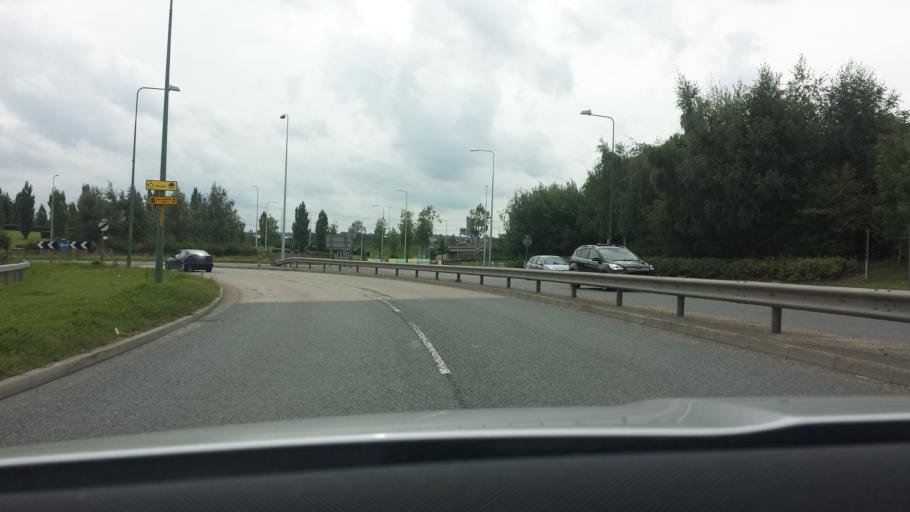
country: GB
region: England
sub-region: Kent
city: Swanscombe
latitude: 51.4329
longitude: 0.3179
